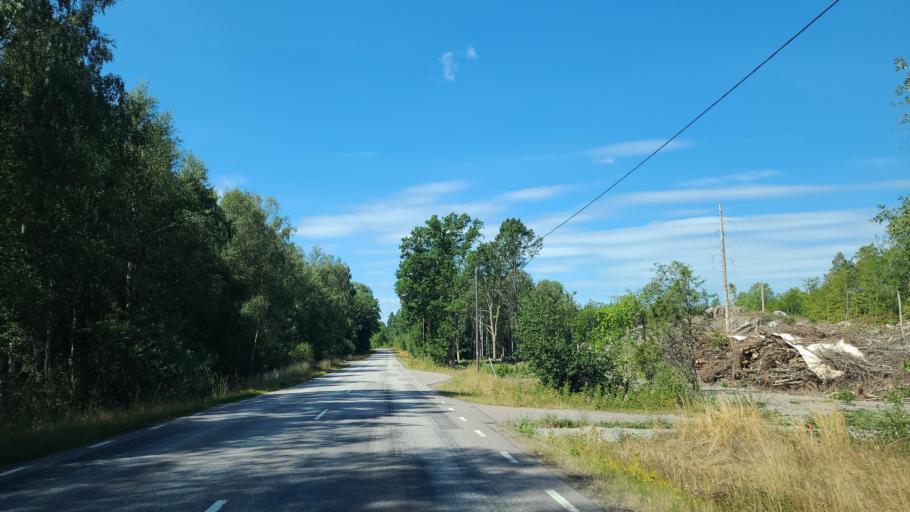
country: SE
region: Kalmar
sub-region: Nybro Kommun
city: Nybro
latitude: 56.5640
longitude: 15.7990
